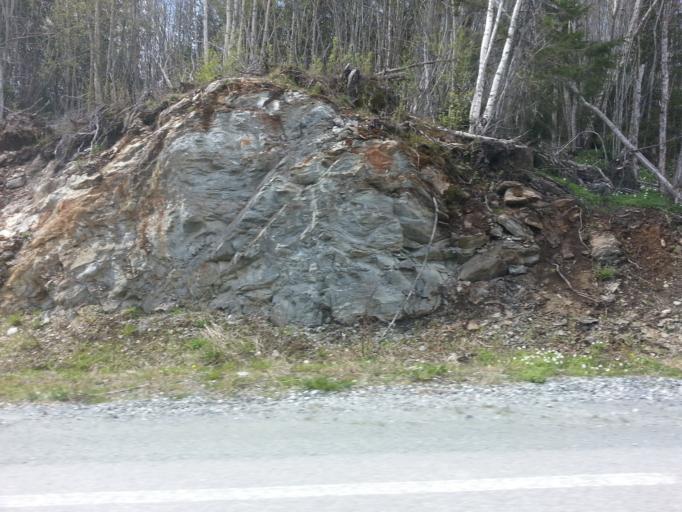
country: NO
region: Nord-Trondelag
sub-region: Levanger
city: Skogn
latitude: 63.6408
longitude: 11.2491
